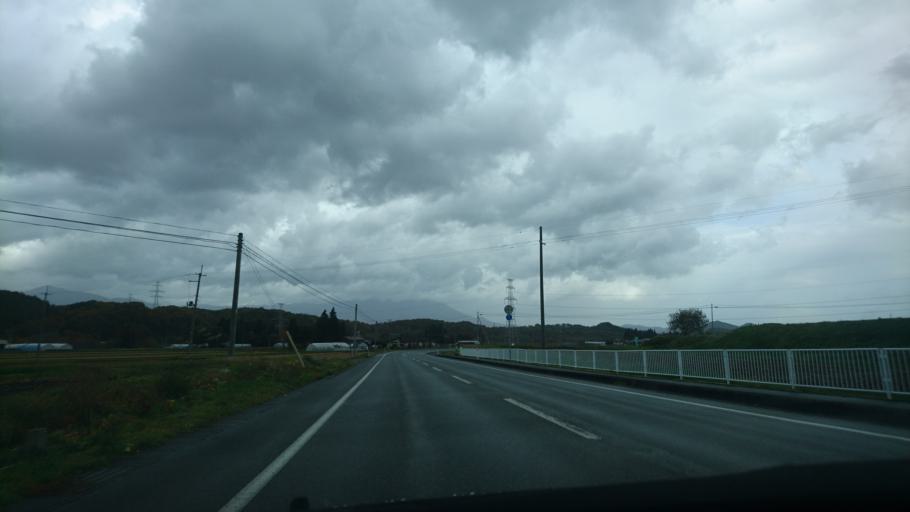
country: JP
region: Iwate
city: Shizukuishi
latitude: 39.6530
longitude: 140.9567
